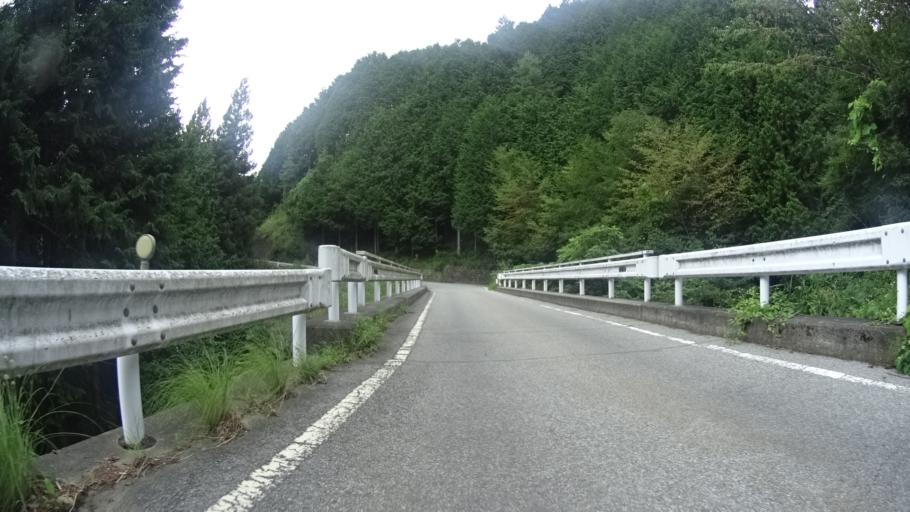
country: JP
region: Yamanashi
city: Enzan
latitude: 35.7881
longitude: 138.6927
